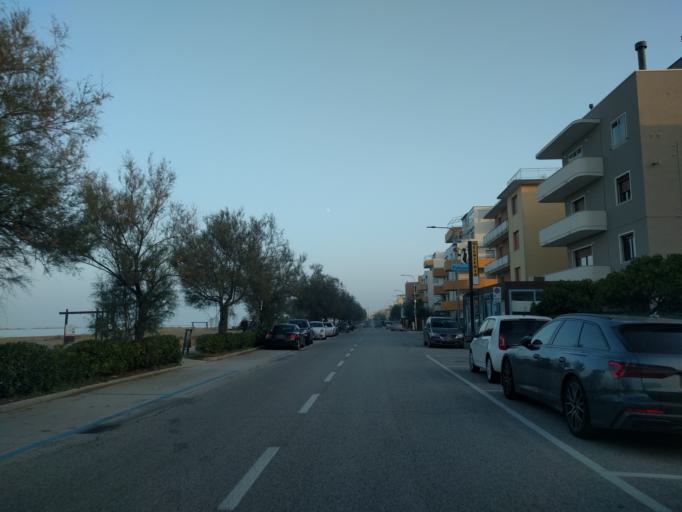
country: IT
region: The Marches
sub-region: Provincia di Ancona
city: Senigallia
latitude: 43.7394
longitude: 13.1877
